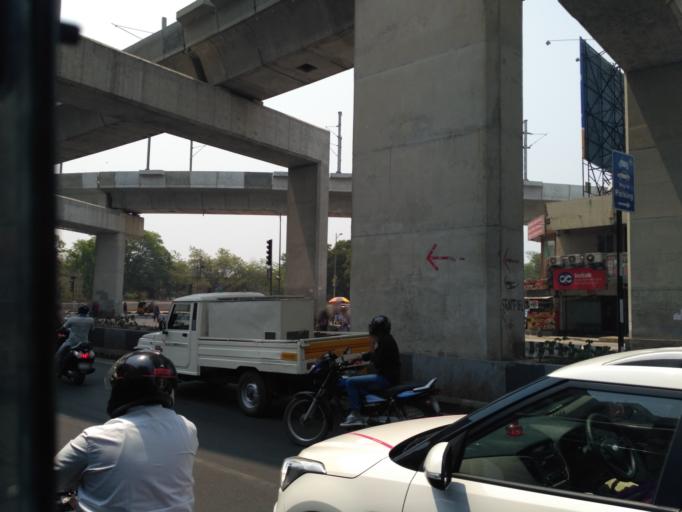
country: IN
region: Telangana
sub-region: Hyderabad
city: Hyderabad
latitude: 17.4375
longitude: 78.4437
